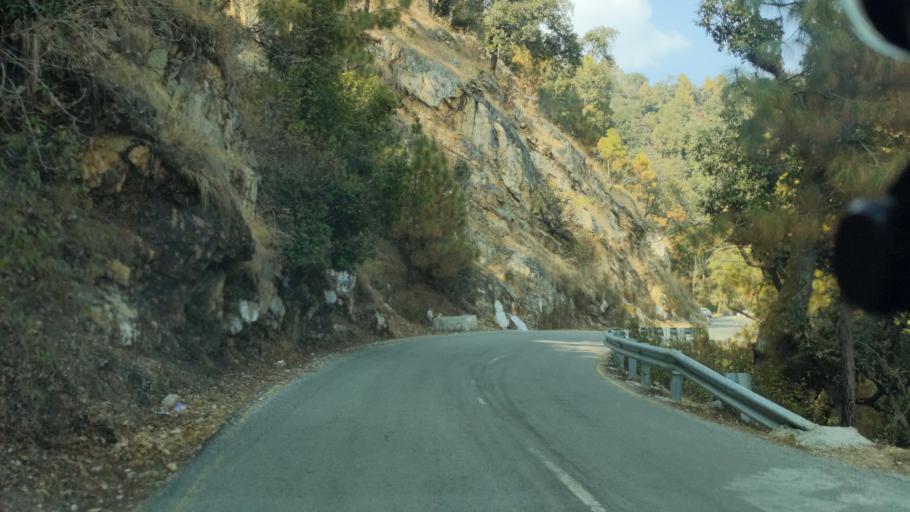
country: IN
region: Uttarakhand
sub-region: Naini Tal
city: Bhowali
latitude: 29.4007
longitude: 79.5347
